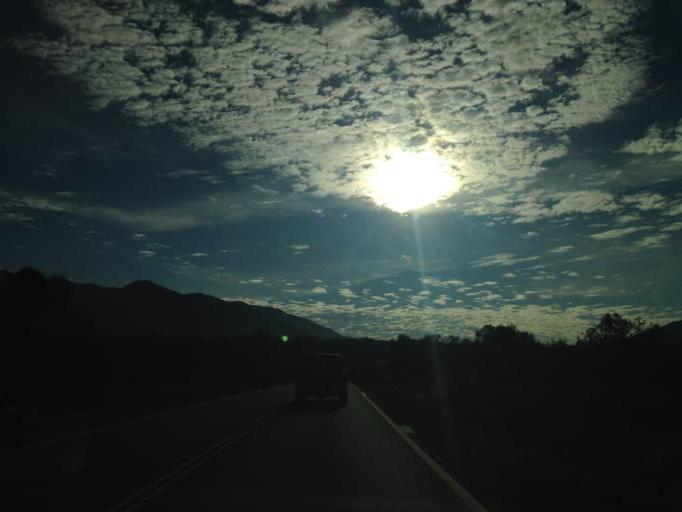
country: US
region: California
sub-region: San Diego County
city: Rainbow
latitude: 33.3615
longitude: -117.0471
